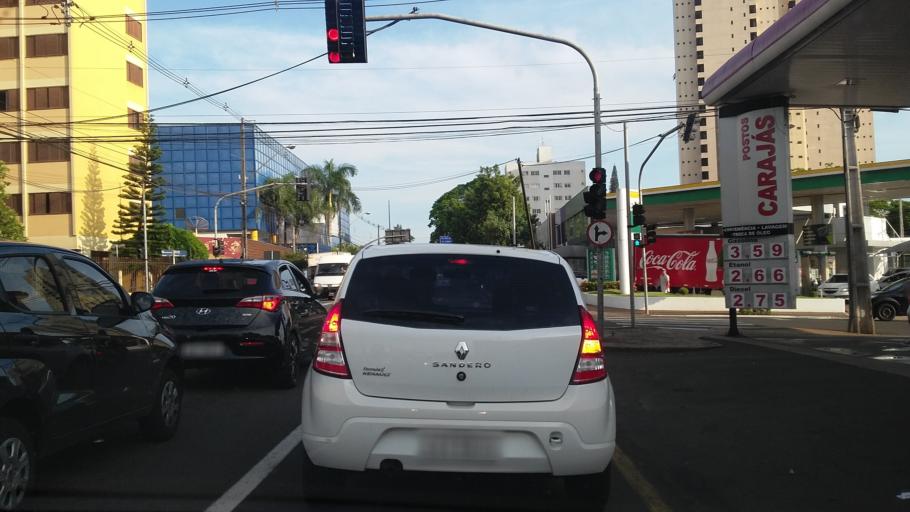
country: BR
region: Parana
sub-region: Londrina
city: Londrina
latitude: -23.3038
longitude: -51.1788
